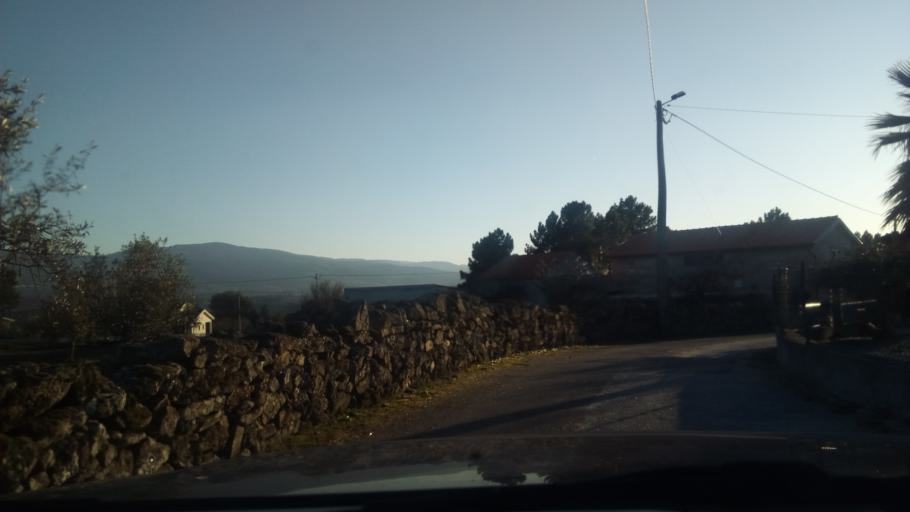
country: PT
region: Guarda
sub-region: Fornos de Algodres
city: Fornos de Algodres
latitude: 40.6053
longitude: -7.5061
